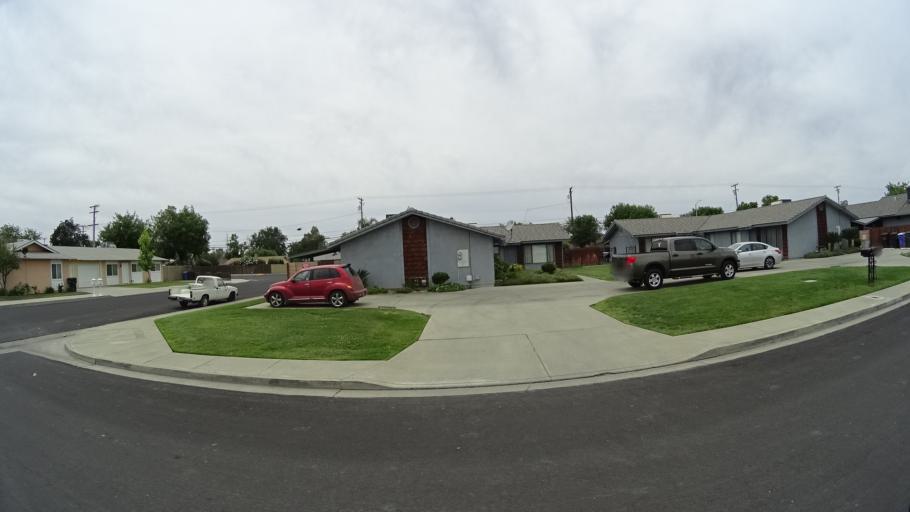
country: US
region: California
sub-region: Kings County
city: Hanford
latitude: 36.3484
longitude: -119.6363
